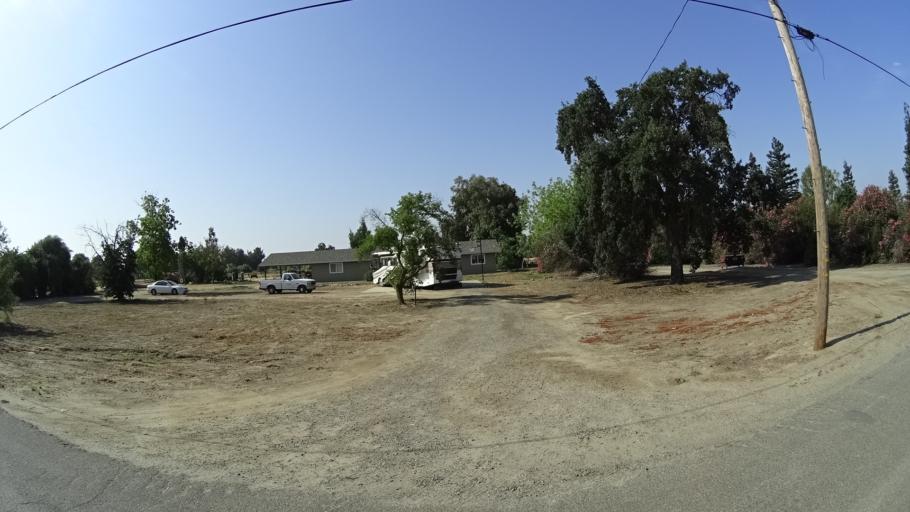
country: US
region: California
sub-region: Kings County
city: Lemoore
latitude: 36.3531
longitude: -119.8371
